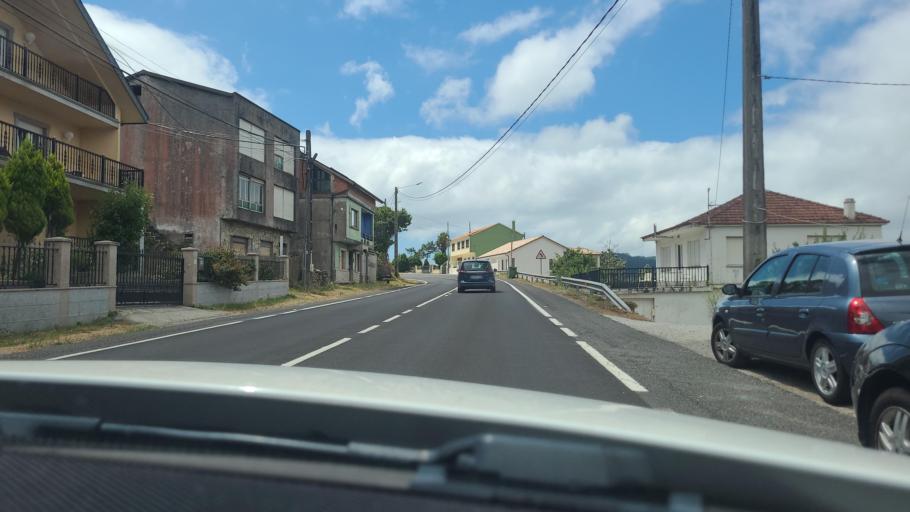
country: ES
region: Galicia
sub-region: Provincia da Coruna
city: Cee
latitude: 42.9427
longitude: -9.1723
